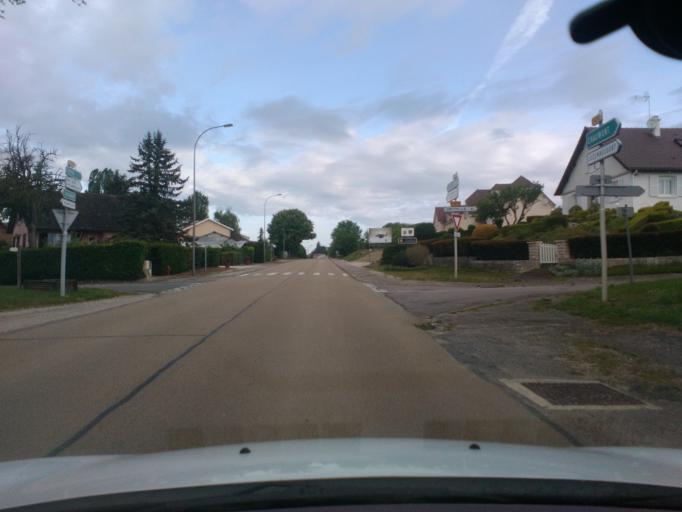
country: FR
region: Champagne-Ardenne
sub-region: Departement de la Haute-Marne
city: Lavilleneuve-au-Roi
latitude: 48.2227
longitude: 4.8940
